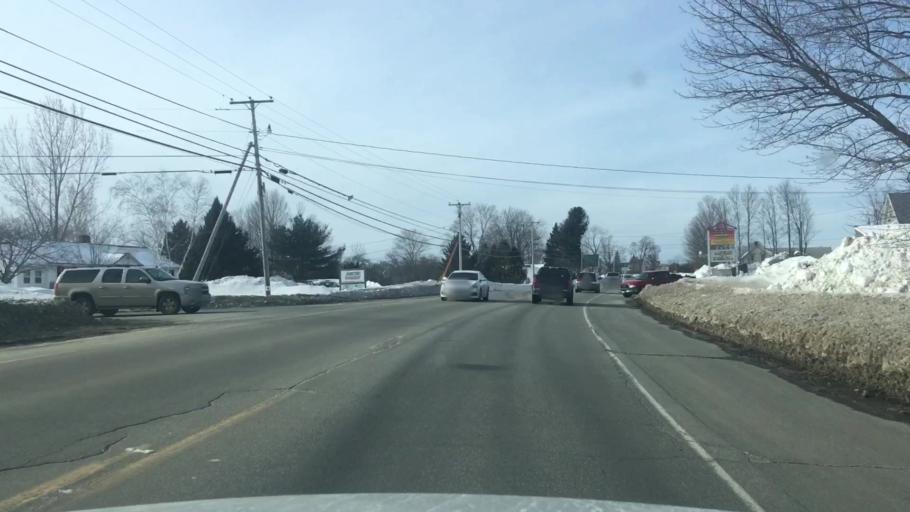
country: US
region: Maine
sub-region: Penobscot County
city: Charleston
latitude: 44.9892
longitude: -69.0140
